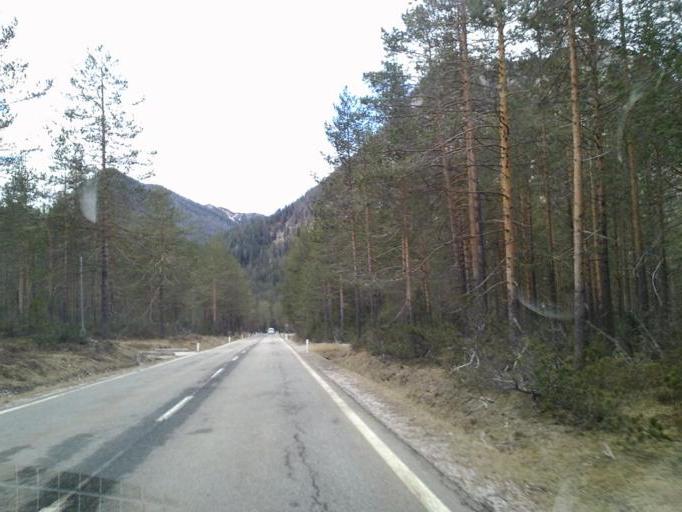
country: IT
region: Trentino-Alto Adige
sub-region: Bolzano
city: Dobbiaco
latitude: 46.6153
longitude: 12.2235
